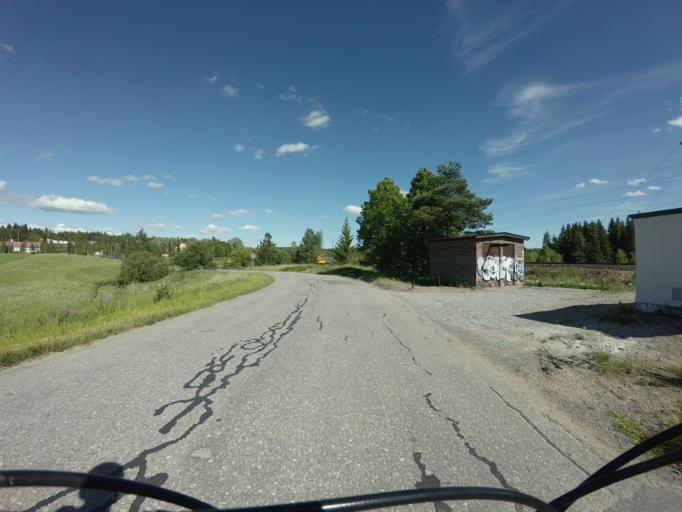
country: FI
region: Varsinais-Suomi
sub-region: Turku
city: Vahto
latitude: 60.5366
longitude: 22.3425
